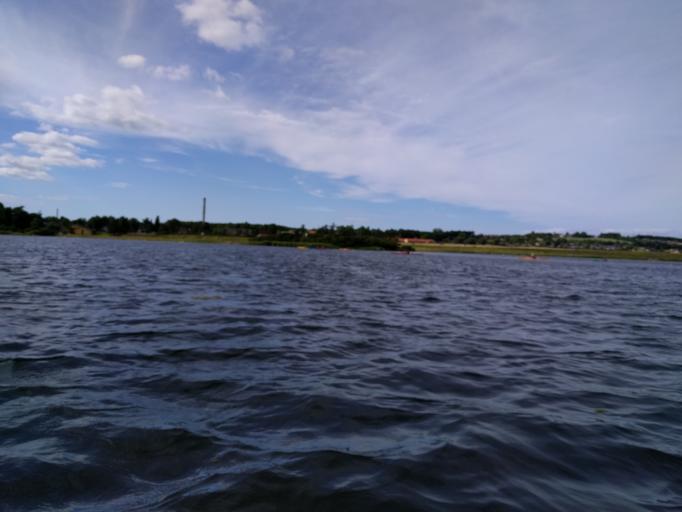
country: DK
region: South Denmark
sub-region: Kerteminde Kommune
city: Munkebo
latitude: 55.4537
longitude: 10.5654
